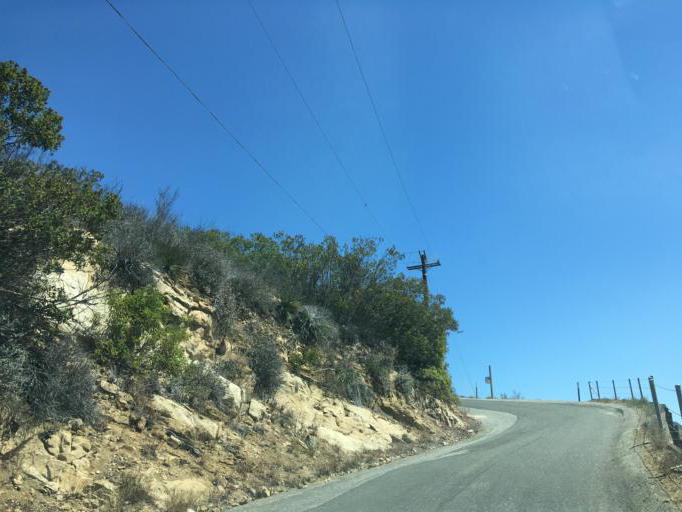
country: US
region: California
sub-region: Los Angeles County
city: Malibu Beach
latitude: 34.0466
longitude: -118.7445
